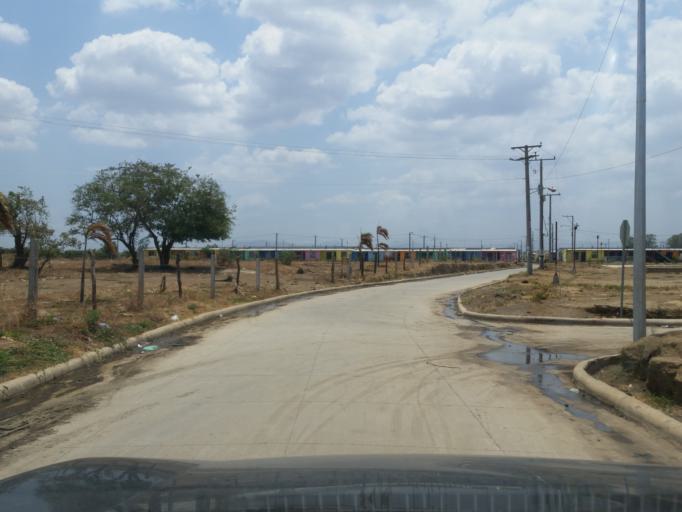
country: NI
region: Managua
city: Tipitapa
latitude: 12.1319
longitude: -86.1566
